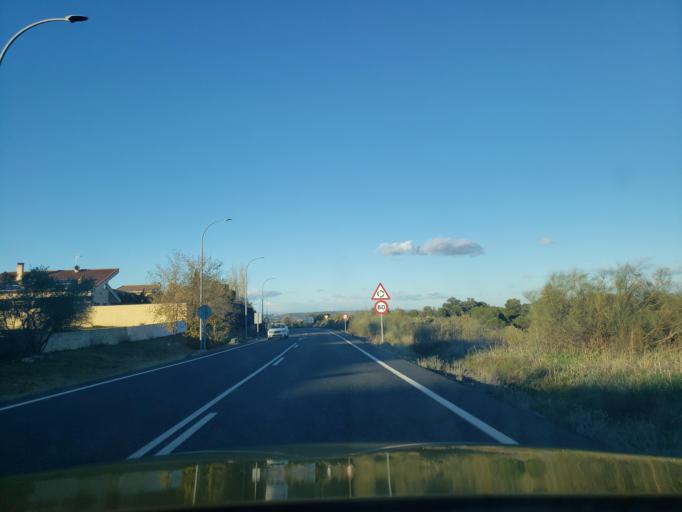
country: ES
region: Castille-La Mancha
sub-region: Province of Toledo
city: Cobisa
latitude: 39.8257
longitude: -4.0181
